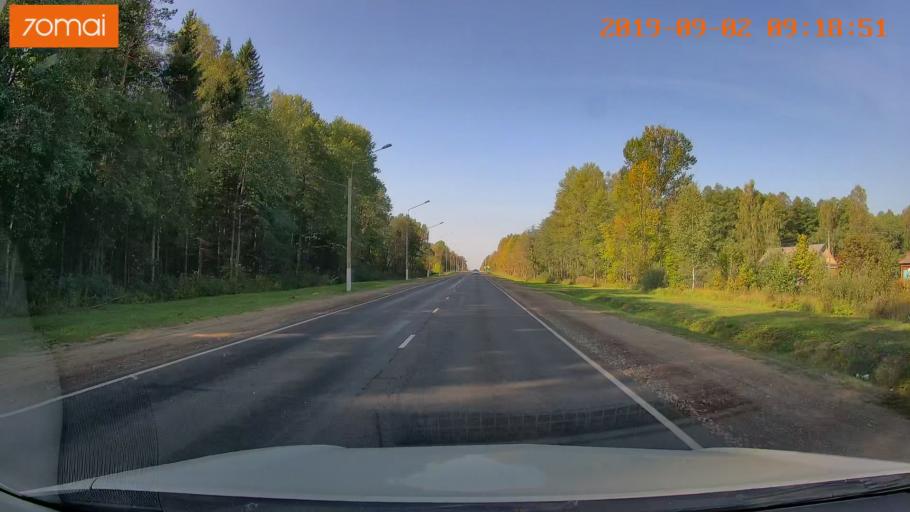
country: RU
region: Kaluga
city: Nikola-Lenivets
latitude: 54.8126
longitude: 35.4184
